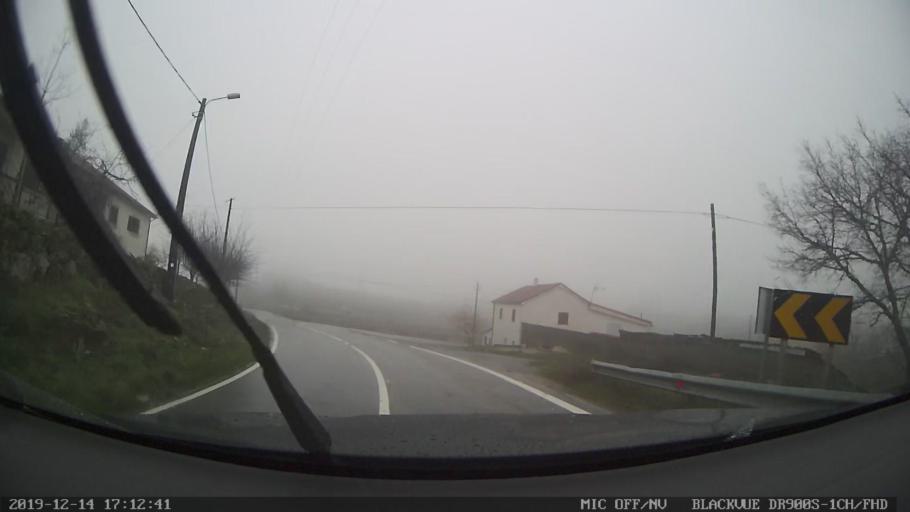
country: PT
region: Vila Real
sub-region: Vila Pouca de Aguiar
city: Vila Pouca de Aguiar
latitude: 41.4957
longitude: -7.6215
